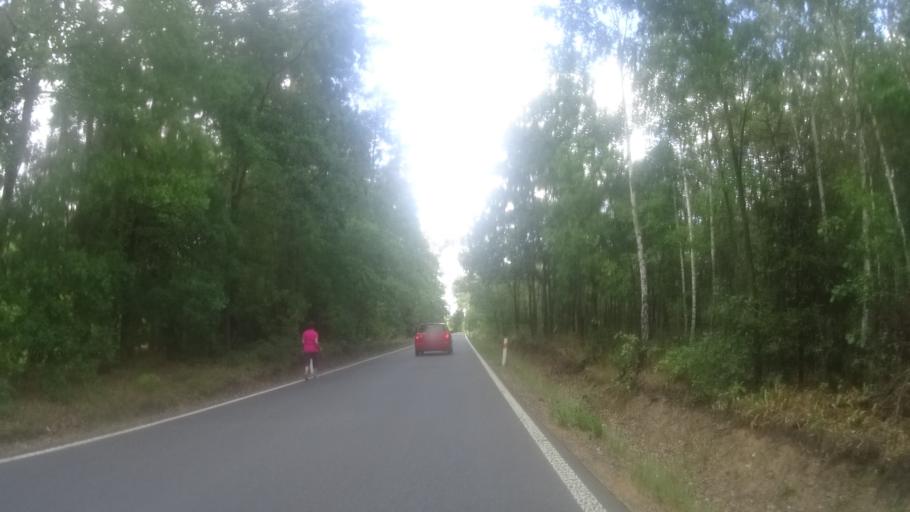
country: CZ
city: Borohradek
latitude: 50.0819
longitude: 16.1181
